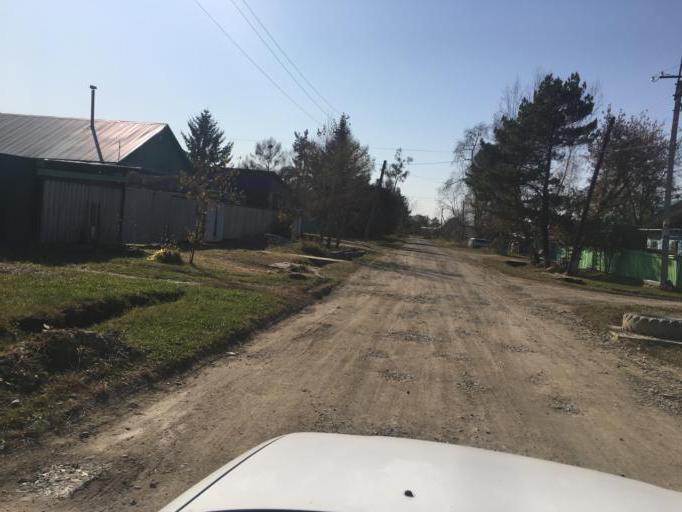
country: RU
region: Primorskiy
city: Dal'nerechensk
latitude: 45.9316
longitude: 133.7528
